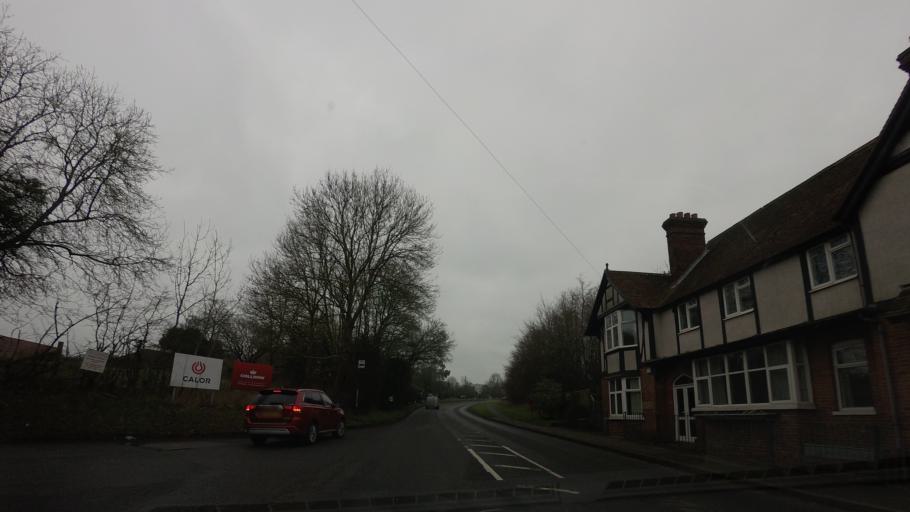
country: GB
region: England
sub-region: Kent
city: Cranbrook
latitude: 51.0828
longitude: 0.5092
